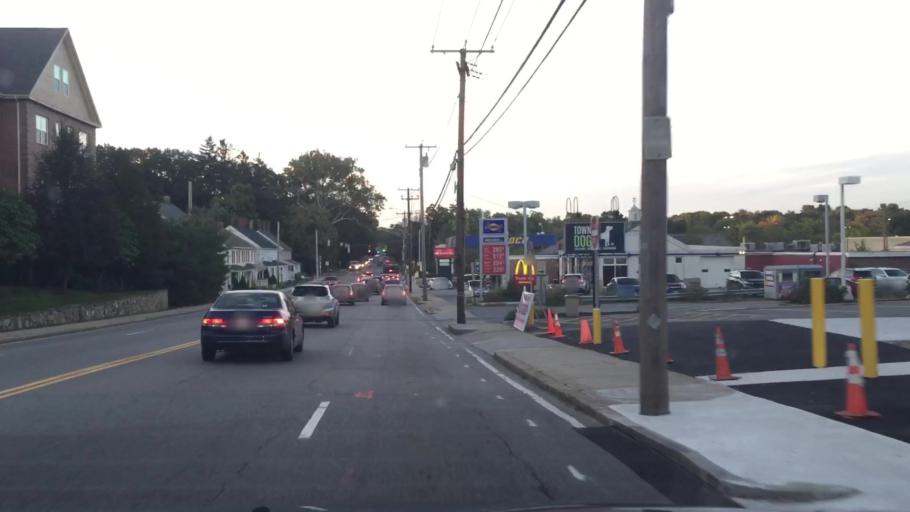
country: US
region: Massachusetts
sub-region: Essex County
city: Andover
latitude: 42.6635
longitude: -71.1452
